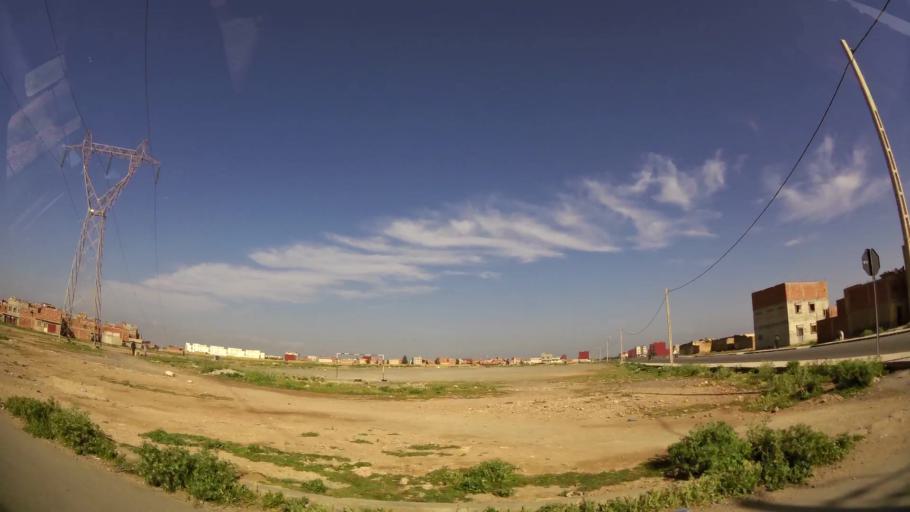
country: MA
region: Oriental
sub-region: Oujda-Angad
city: Oujda
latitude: 34.7220
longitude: -1.8919
